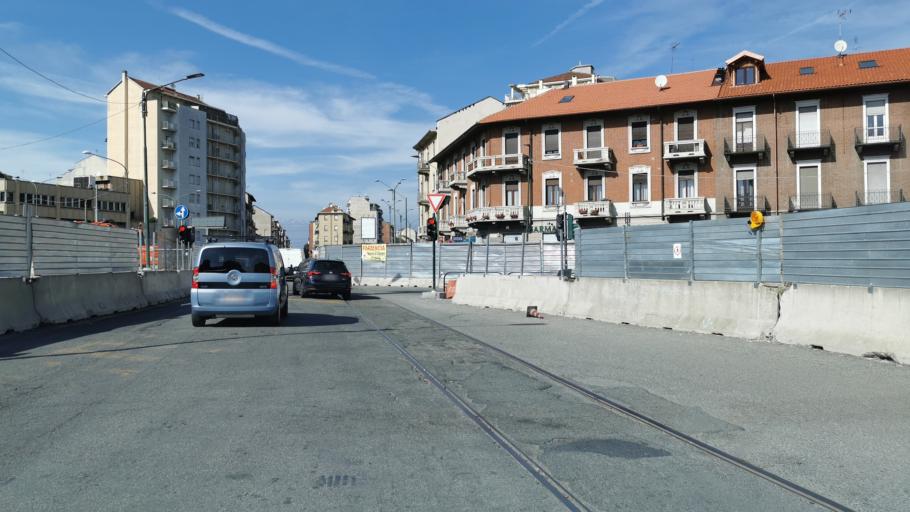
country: IT
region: Piedmont
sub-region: Provincia di Torino
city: Venaria Reale
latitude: 45.1052
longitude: 7.6638
